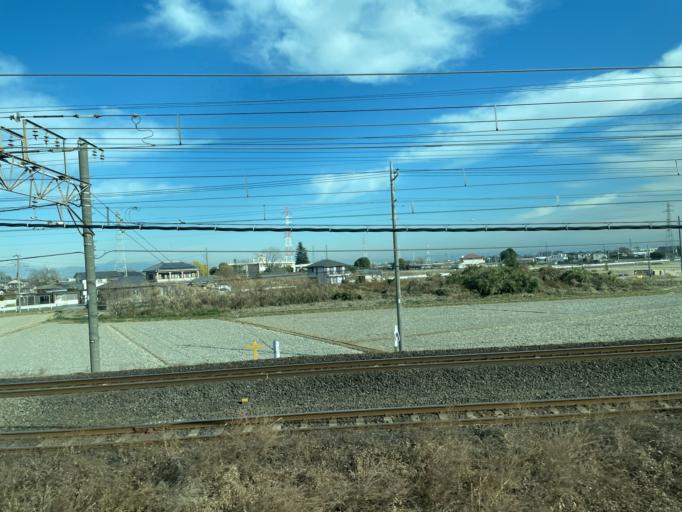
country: JP
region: Saitama
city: Kumagaya
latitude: 36.1644
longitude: 139.3496
